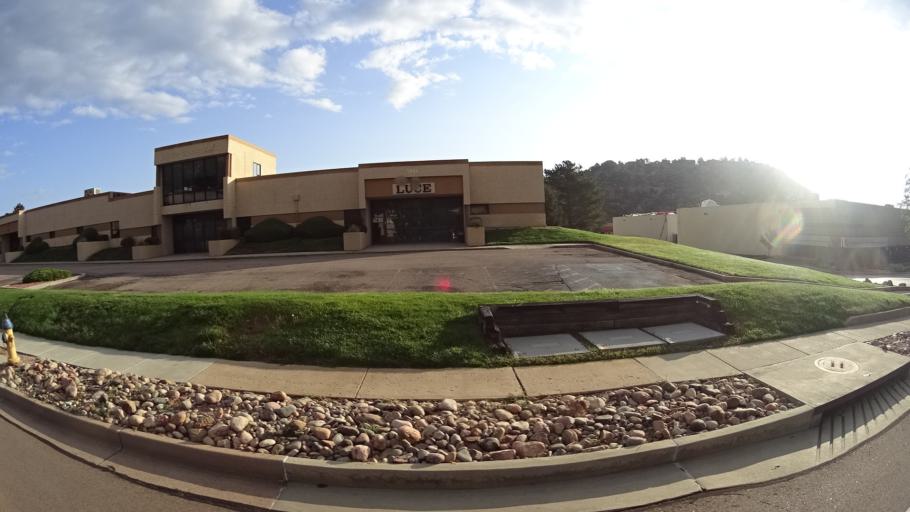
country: US
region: Colorado
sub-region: El Paso County
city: Manitou Springs
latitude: 38.9021
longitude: -104.8552
